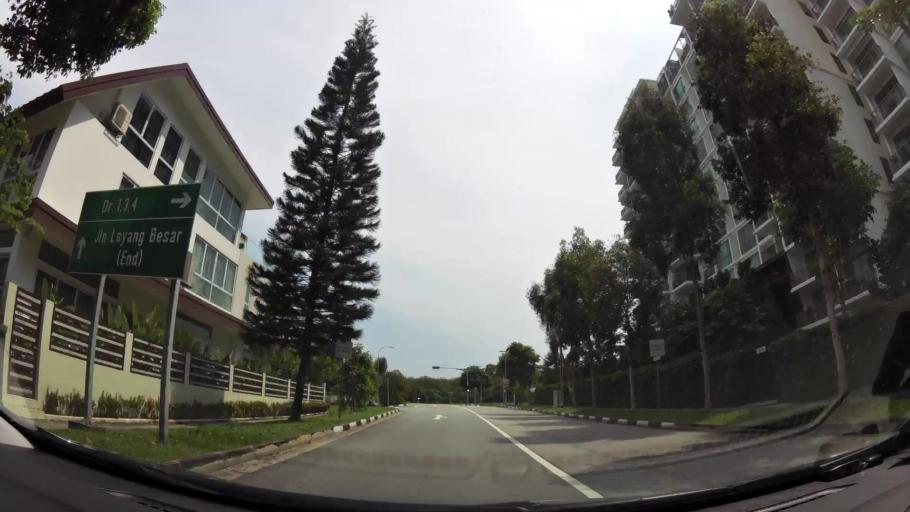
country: MY
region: Johor
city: Kampung Pasir Gudang Baru
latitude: 1.3788
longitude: 103.9613
